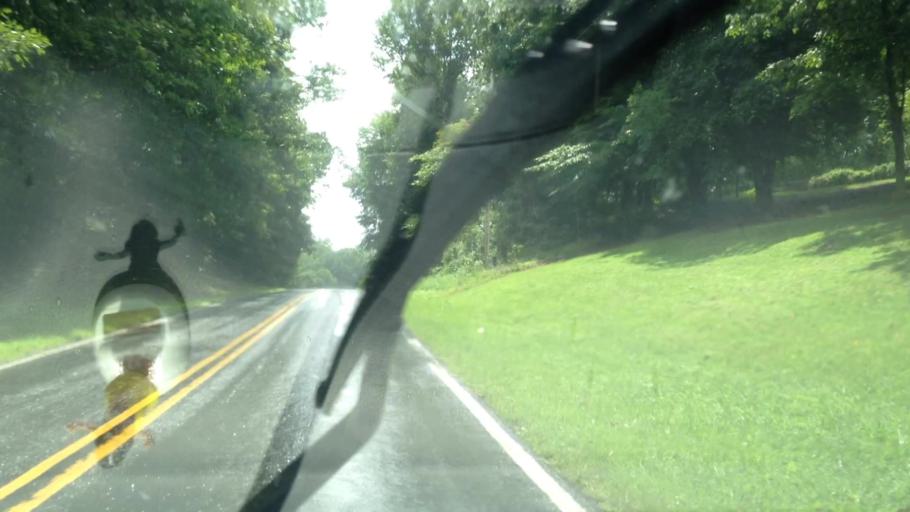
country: US
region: North Carolina
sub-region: Forsyth County
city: Walkertown
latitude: 36.2130
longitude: -80.1124
